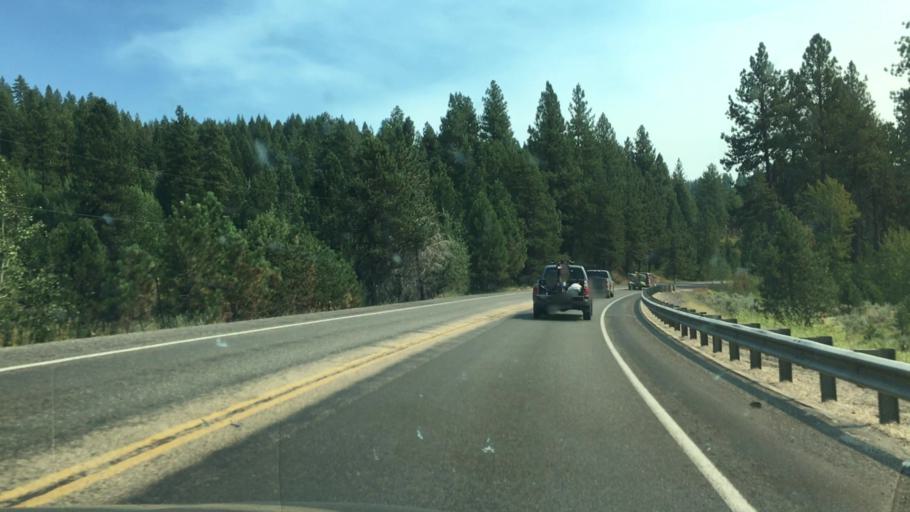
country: US
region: Idaho
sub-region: Valley County
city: Cascade
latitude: 44.5946
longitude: -116.0412
